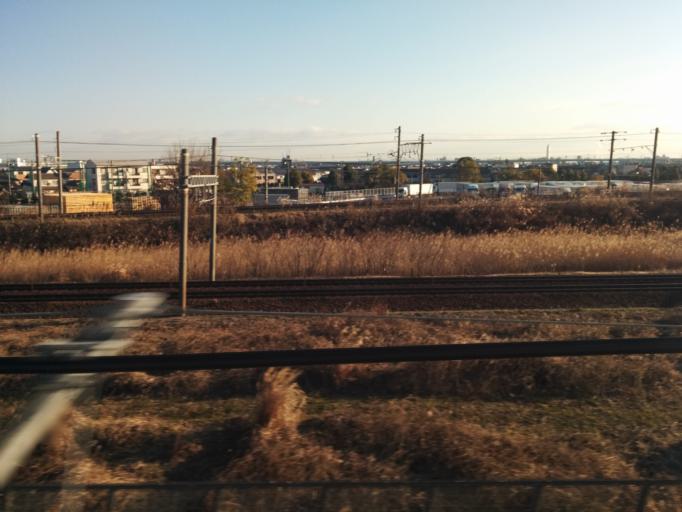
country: JP
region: Aichi
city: Nagoya-shi
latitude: 35.2132
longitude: 136.8450
